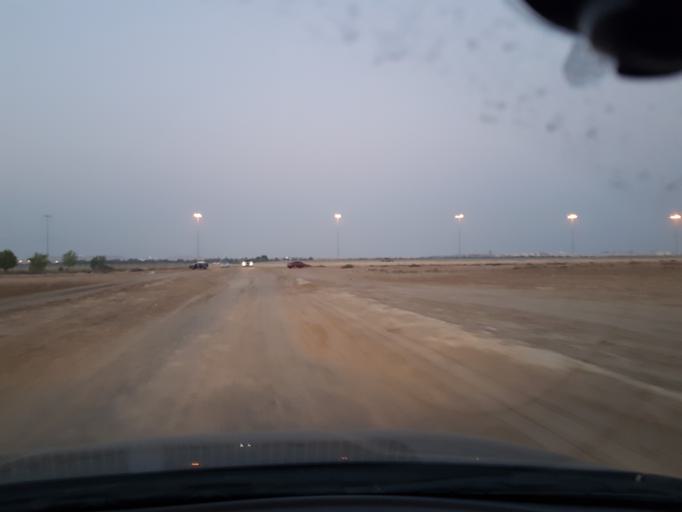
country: BH
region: Central Governorate
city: Dar Kulayb
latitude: 26.0104
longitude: 50.4821
